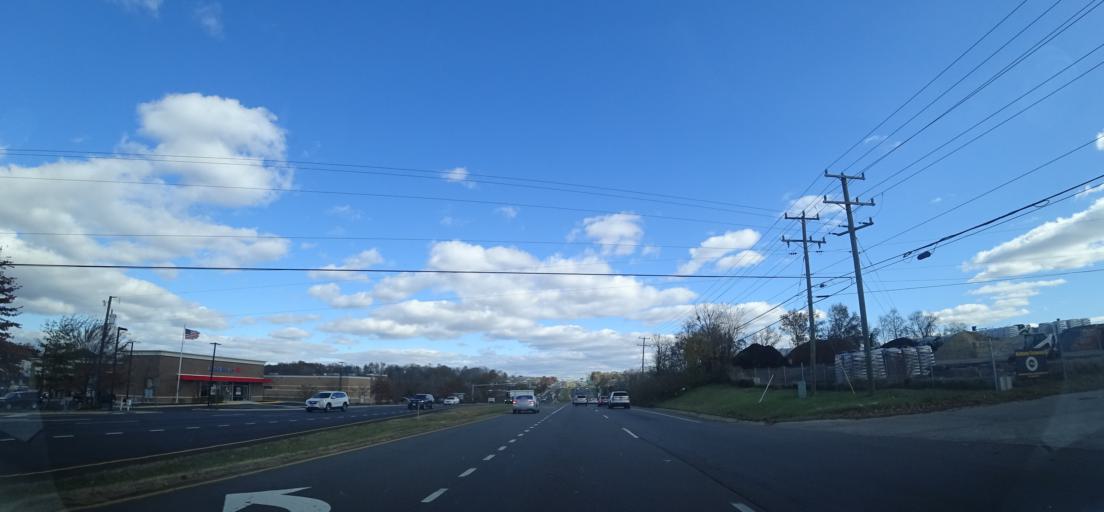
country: US
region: Virginia
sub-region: Prince William County
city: Gainesville
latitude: 38.7918
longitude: -77.6282
